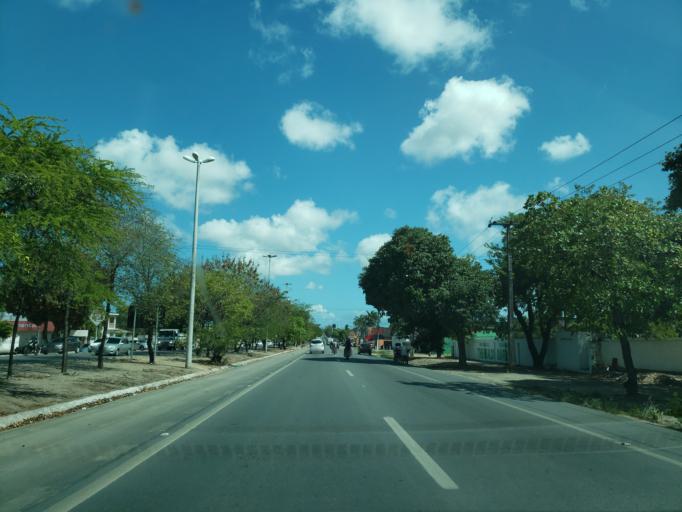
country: BR
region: Alagoas
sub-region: Satuba
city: Satuba
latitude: -9.5414
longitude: -35.7908
